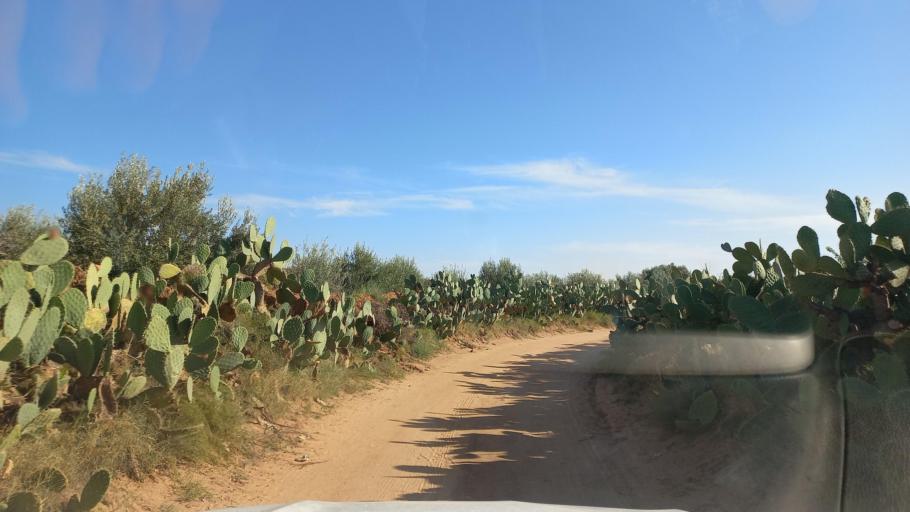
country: TN
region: Al Qasrayn
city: Sbiba
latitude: 35.3337
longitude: 9.1254
